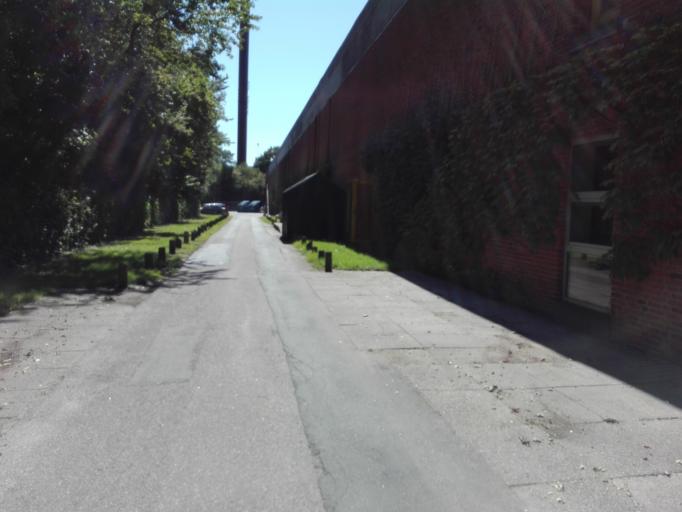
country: DK
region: Central Jutland
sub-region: Arhus Kommune
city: Tranbjerg
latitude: 56.1081
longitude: 10.1430
